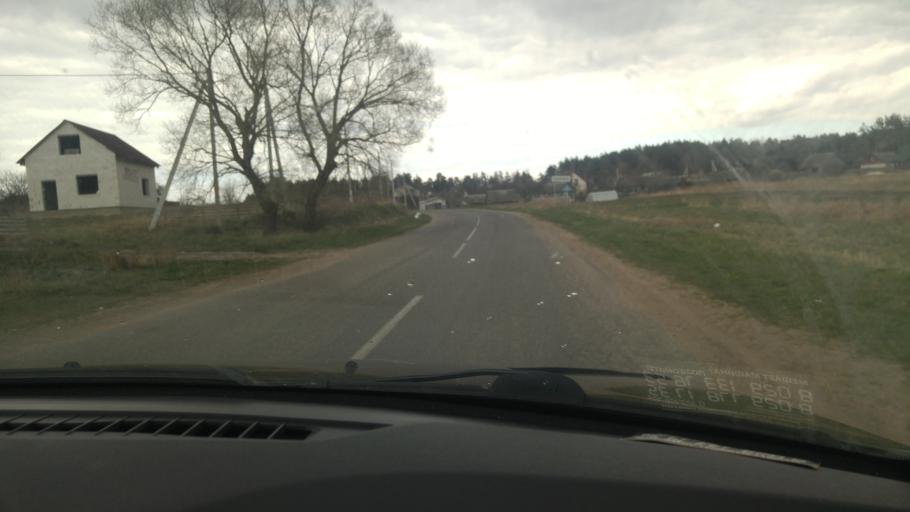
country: BY
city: Michanovichi
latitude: 53.6191
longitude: 27.7291
